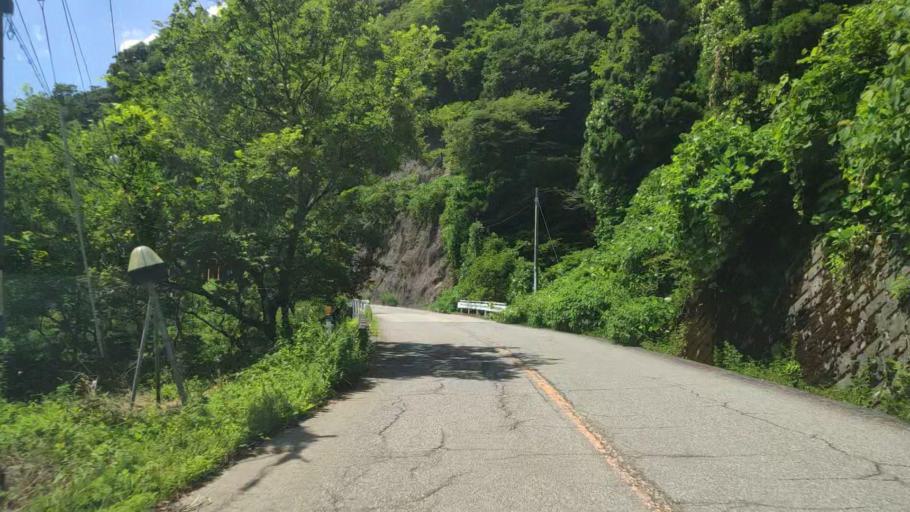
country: JP
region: Fukui
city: Ono
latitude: 35.9251
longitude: 136.5458
